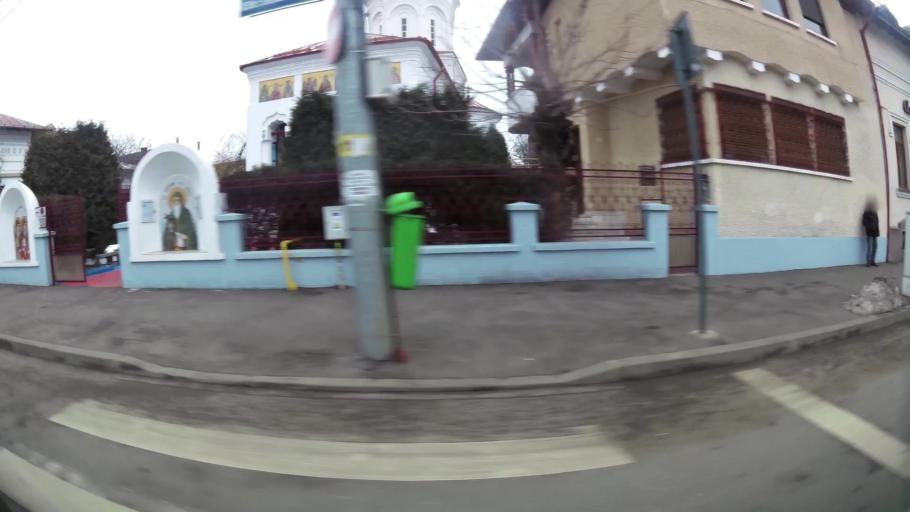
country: RO
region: Prahova
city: Ploiesti
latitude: 44.9367
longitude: 26.0294
